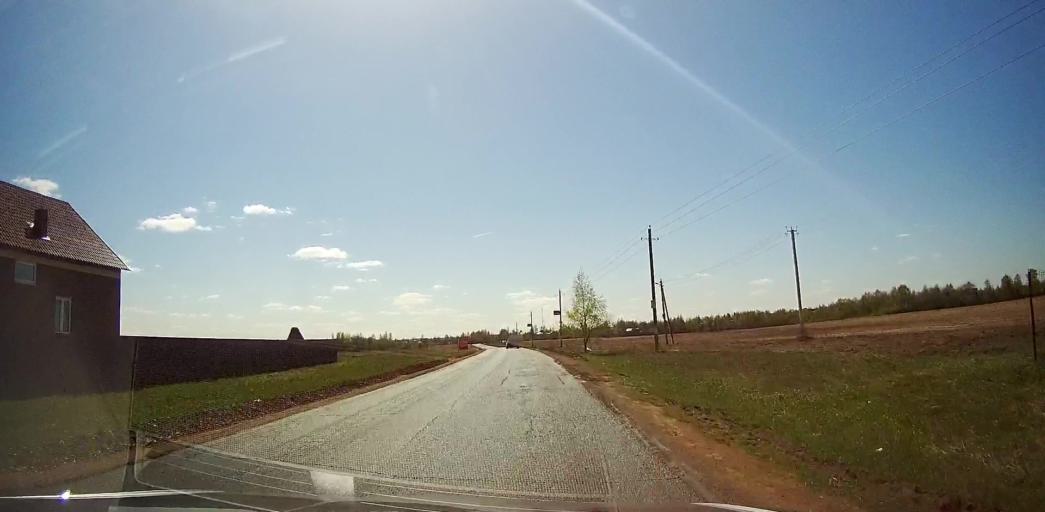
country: RU
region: Moskovskaya
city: Malyshevo
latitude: 55.4661
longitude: 38.3849
